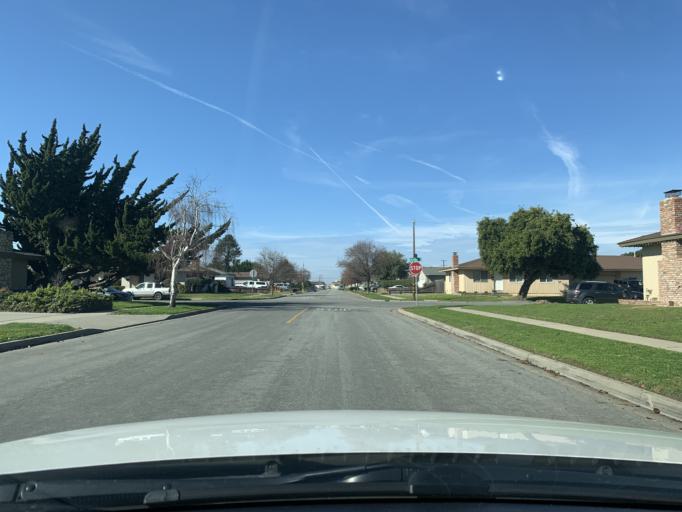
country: US
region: California
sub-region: Monterey County
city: Salinas
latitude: 36.6718
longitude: -121.6766
